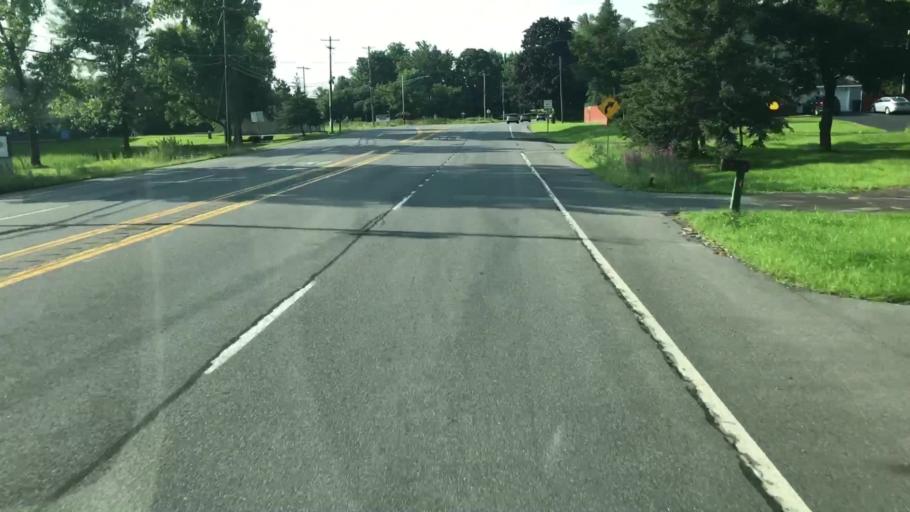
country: US
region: New York
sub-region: Onondaga County
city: Liverpool
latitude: 43.1168
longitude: -76.2051
